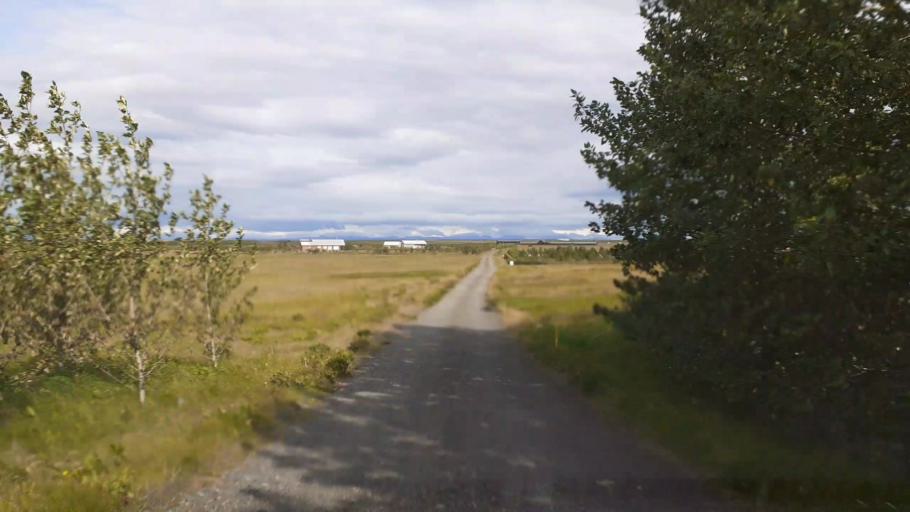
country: IS
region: South
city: Vestmannaeyjar
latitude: 63.7701
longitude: -20.2970
